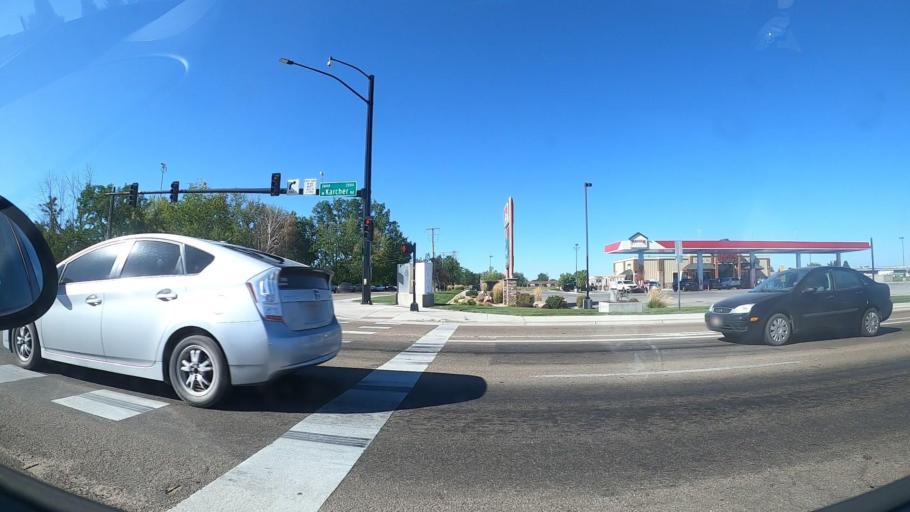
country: US
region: Idaho
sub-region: Canyon County
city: Nampa
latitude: 43.6050
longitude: -116.6121
